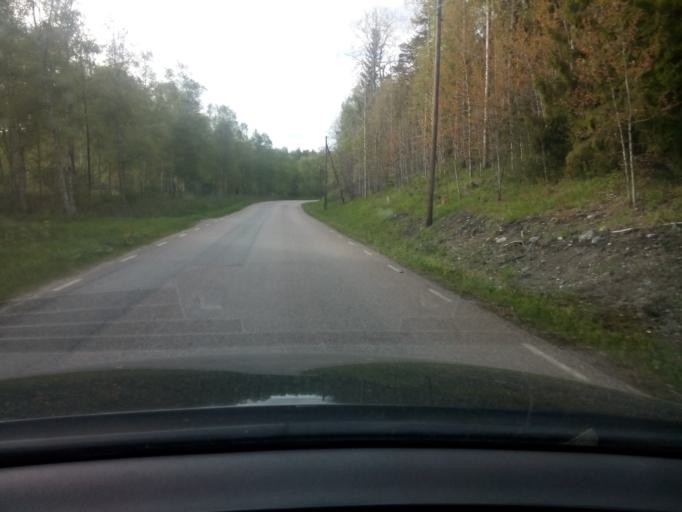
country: SE
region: Soedermanland
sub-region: Nykopings Kommun
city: Stigtomta
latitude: 58.8951
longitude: 16.8911
